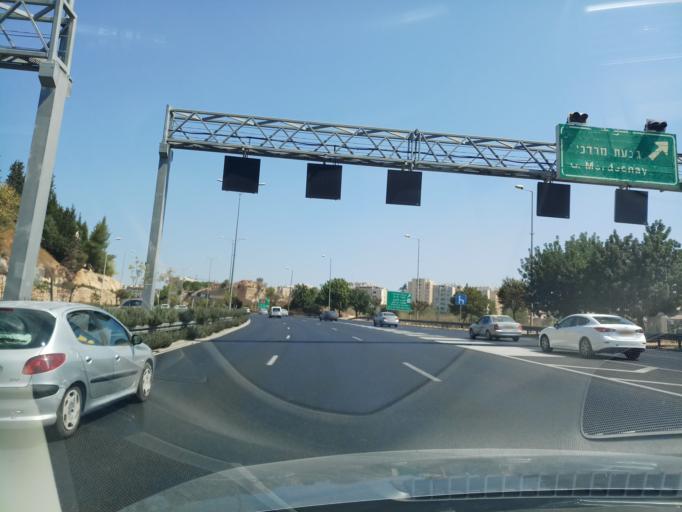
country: IL
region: Jerusalem
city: Jerusalem
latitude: 31.7600
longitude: 35.1939
